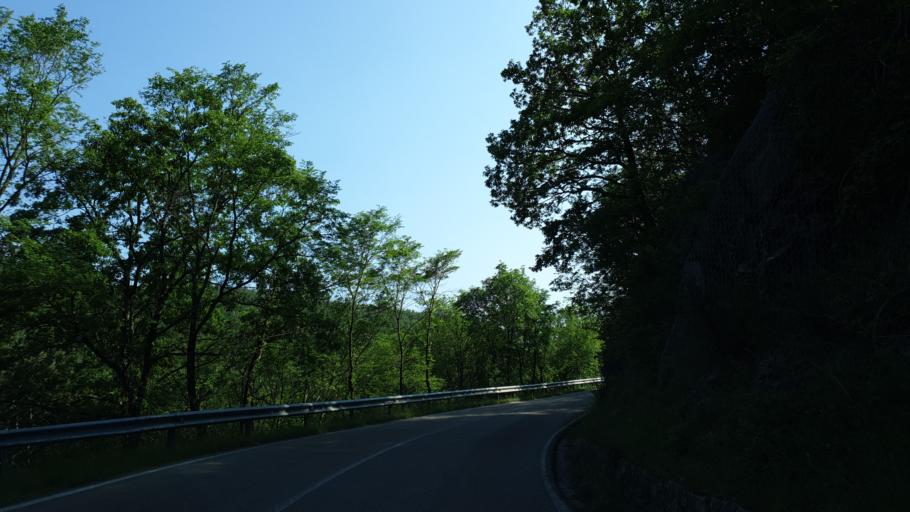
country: IT
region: Tuscany
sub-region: Province of Arezzo
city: Soci
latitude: 43.7639
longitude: 11.8365
